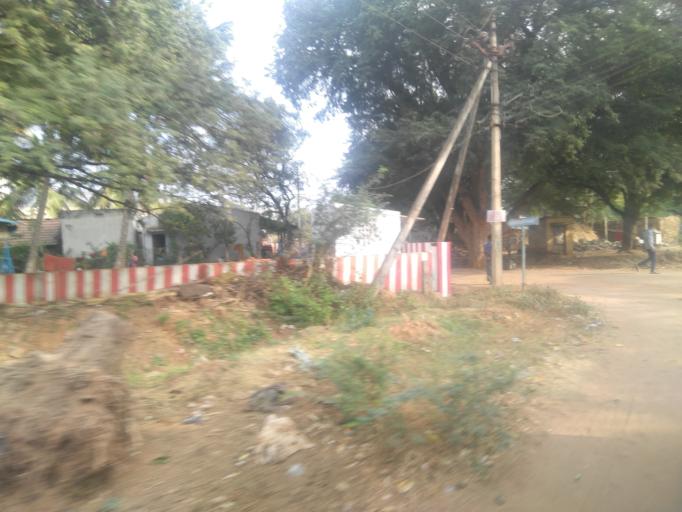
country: IN
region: Tamil Nadu
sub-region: Coimbatore
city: Coimbatore
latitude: 11.0554
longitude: 76.9019
